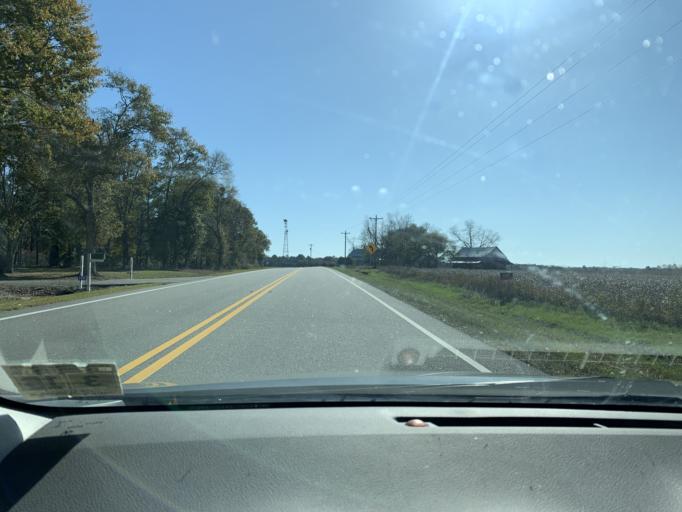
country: US
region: Georgia
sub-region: Ben Hill County
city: Fitzgerald
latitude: 31.7105
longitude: -83.1675
